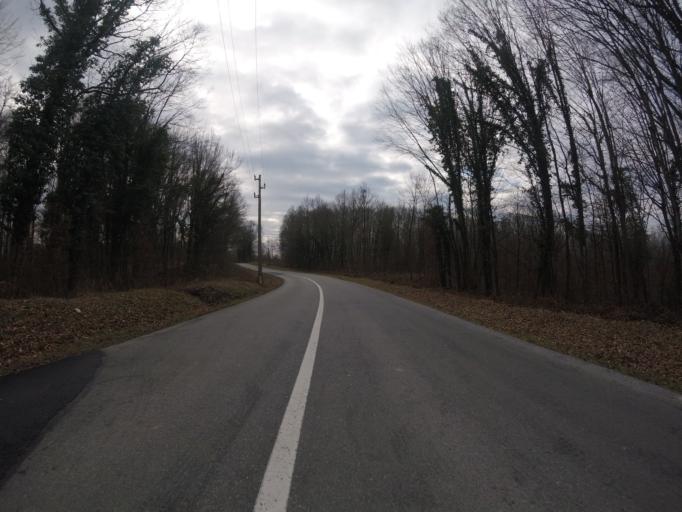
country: HR
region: Zagrebacka
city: Mraclin
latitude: 45.5467
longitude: 16.0557
